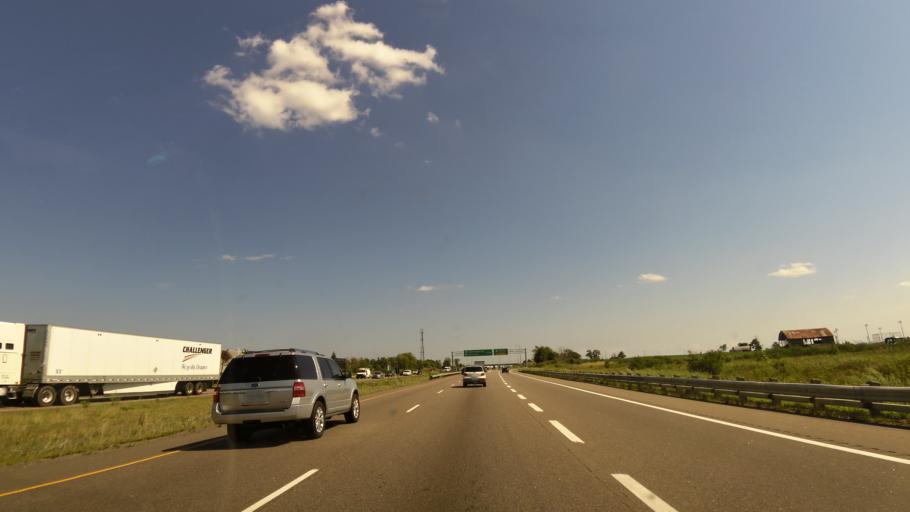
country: CA
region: Ontario
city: Oakville
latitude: 43.5159
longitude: -79.7007
